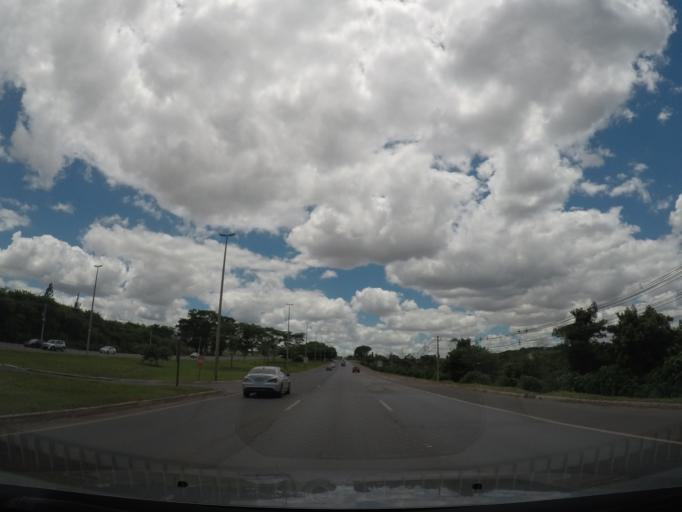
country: BR
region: Federal District
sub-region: Brasilia
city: Brasilia
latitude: -15.7297
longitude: -47.9107
